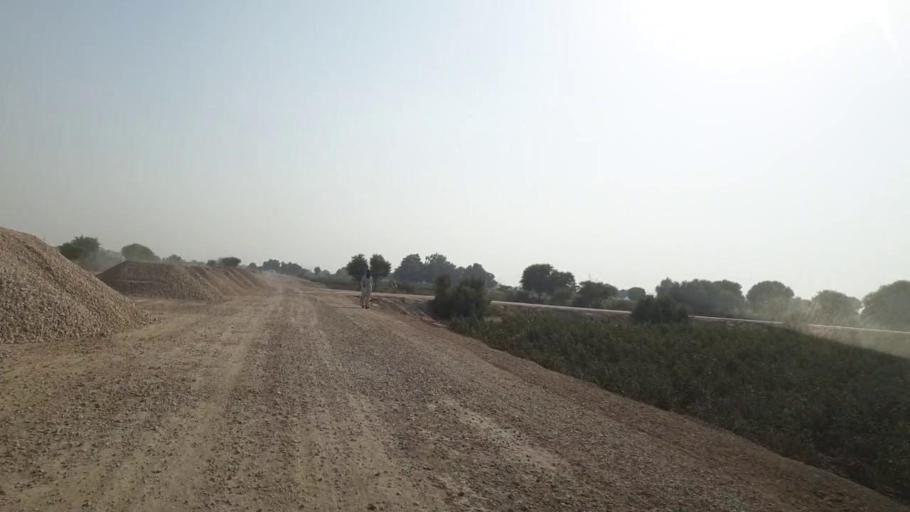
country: PK
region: Sindh
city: Bhan
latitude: 26.4987
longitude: 67.7812
